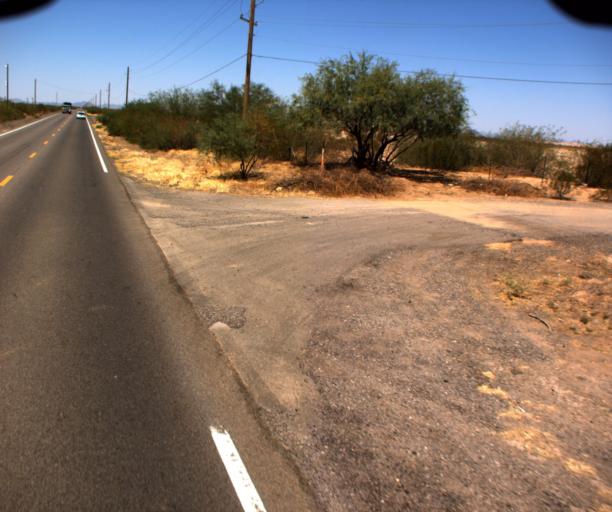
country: US
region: Arizona
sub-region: Pinal County
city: Maricopa
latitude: 33.0686
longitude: -112.2199
